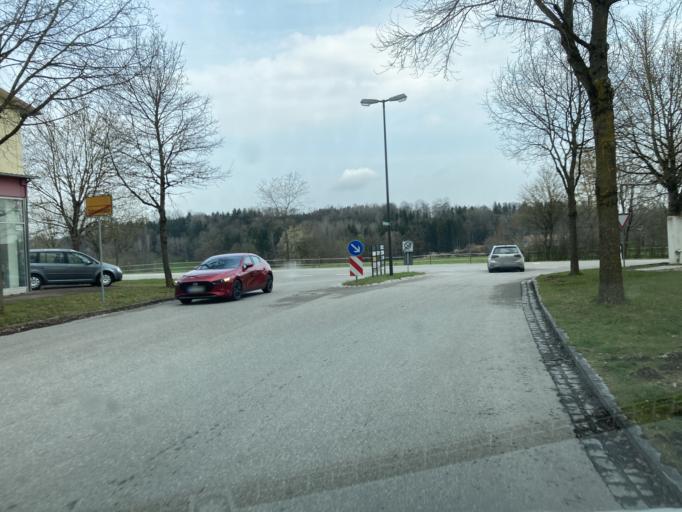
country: DE
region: Bavaria
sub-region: Upper Bavaria
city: Grafing bei Munchen
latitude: 48.0359
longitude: 11.9422
